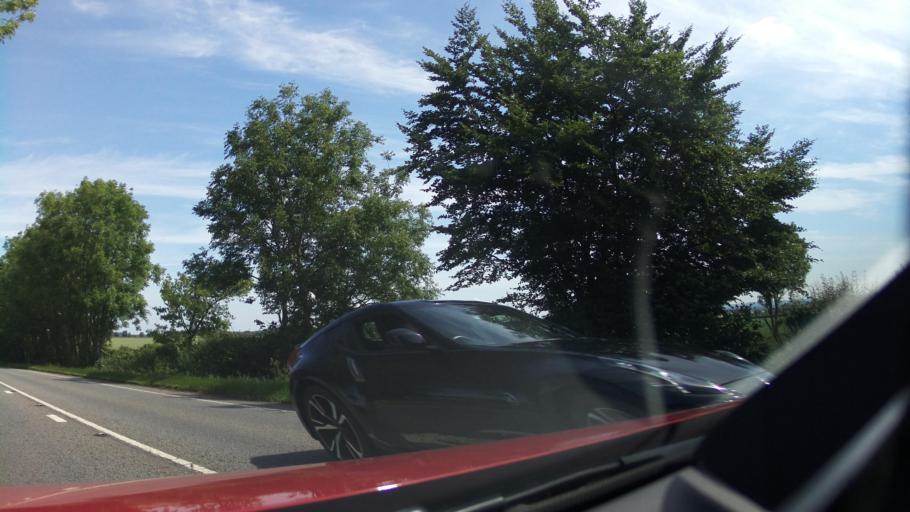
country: GB
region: England
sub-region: Lincolnshire
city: Burton
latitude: 53.3480
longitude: -0.5446
